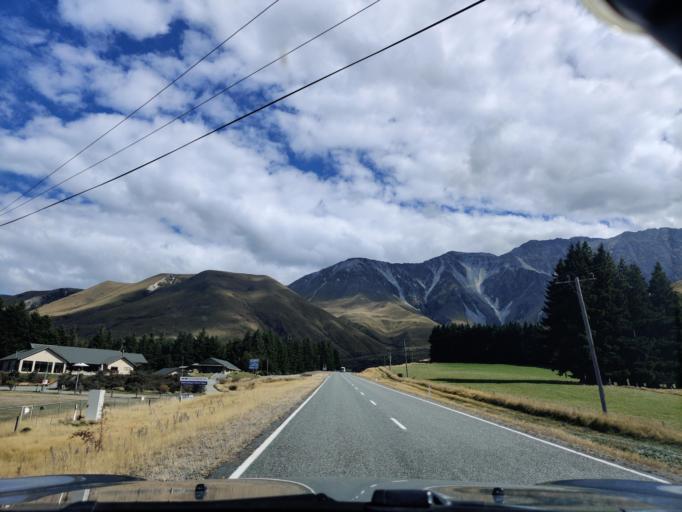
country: NZ
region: Canterbury
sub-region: Timaru District
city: Pleasant Point
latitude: -43.9106
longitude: 170.1221
